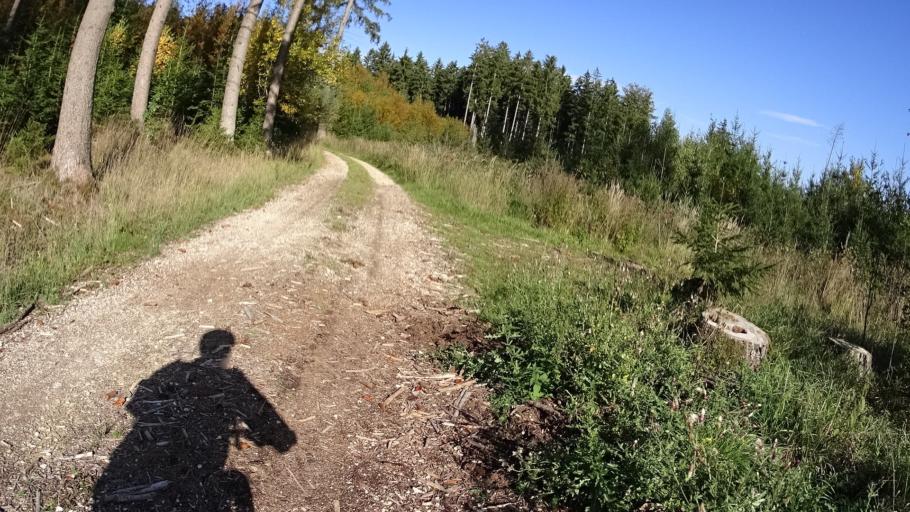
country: DE
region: Bavaria
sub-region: Upper Bavaria
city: Bohmfeld
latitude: 48.8838
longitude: 11.3631
